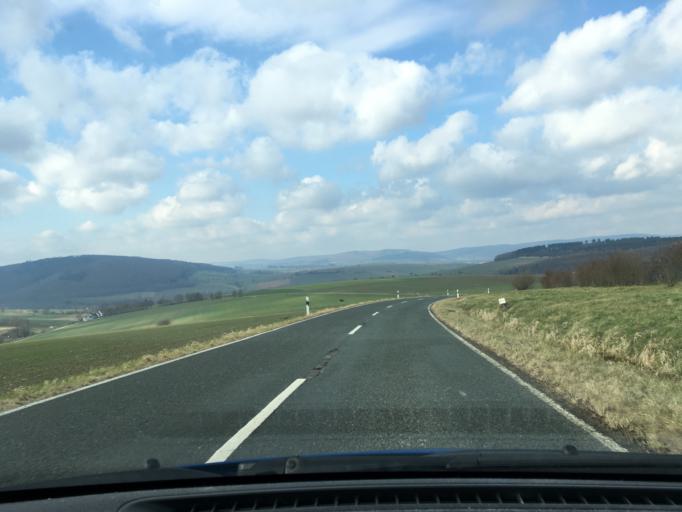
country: DE
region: Lower Saxony
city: Uslar
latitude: 51.6105
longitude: 9.6312
